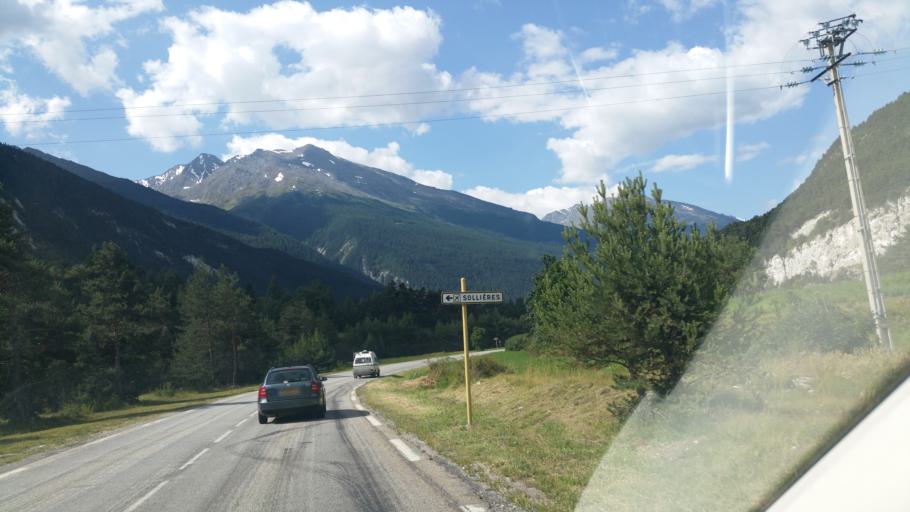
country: FR
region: Rhone-Alpes
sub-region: Departement de la Savoie
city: Modane
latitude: 45.2466
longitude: 6.7969
